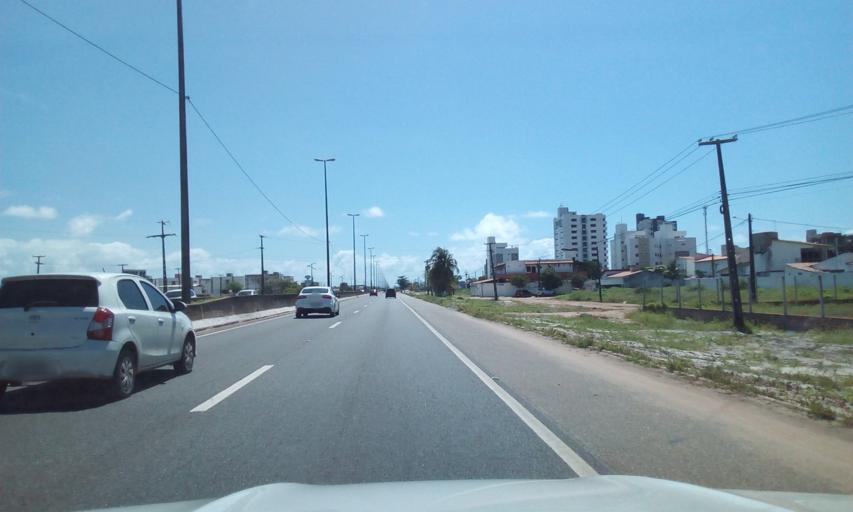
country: BR
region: Paraiba
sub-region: Cabedelo
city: Cabedelo
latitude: -7.0394
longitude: -34.8445
